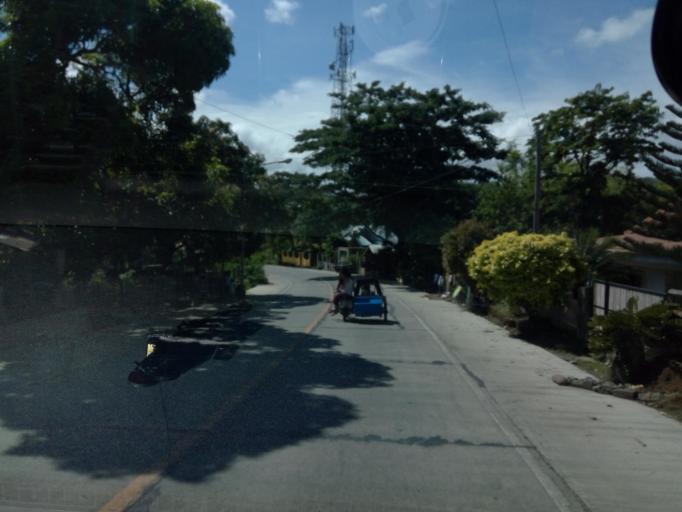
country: PH
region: Central Luzon
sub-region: Province of Nueva Ecija
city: Pantabangan
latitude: 15.8048
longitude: 121.1480
